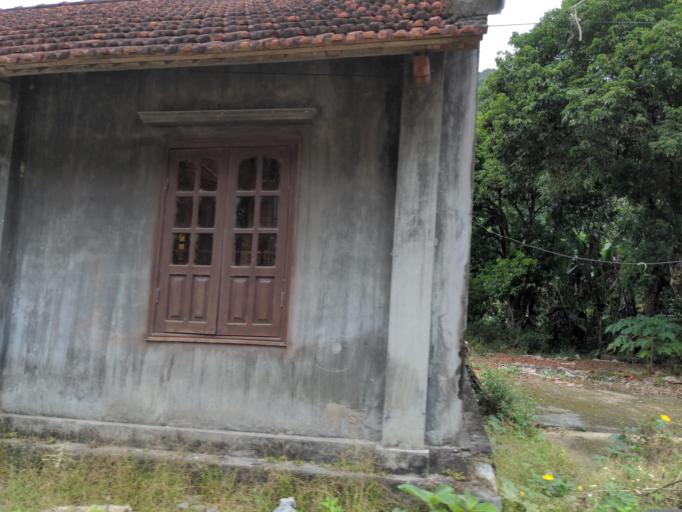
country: VN
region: Hai Phong
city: Cat Ba
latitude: 20.7990
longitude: 107.0422
